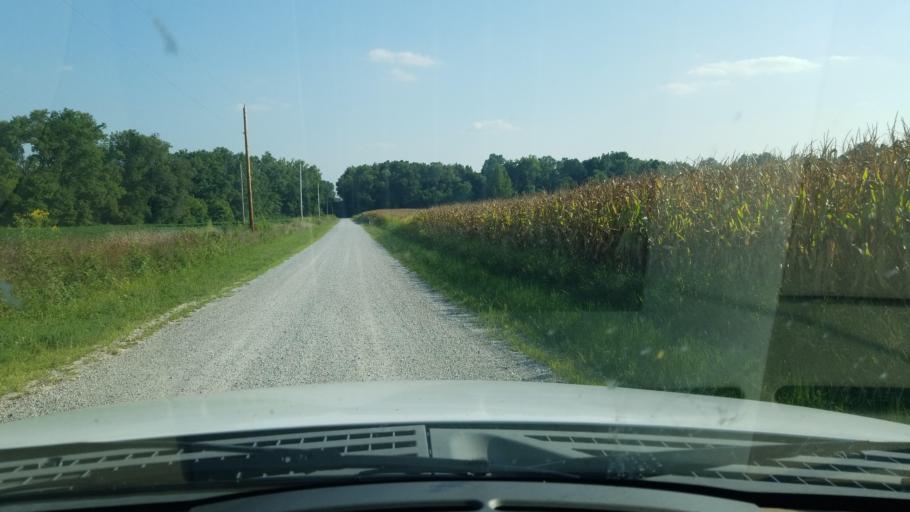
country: US
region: Illinois
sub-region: Saline County
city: Eldorado
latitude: 37.8342
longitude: -88.5027
